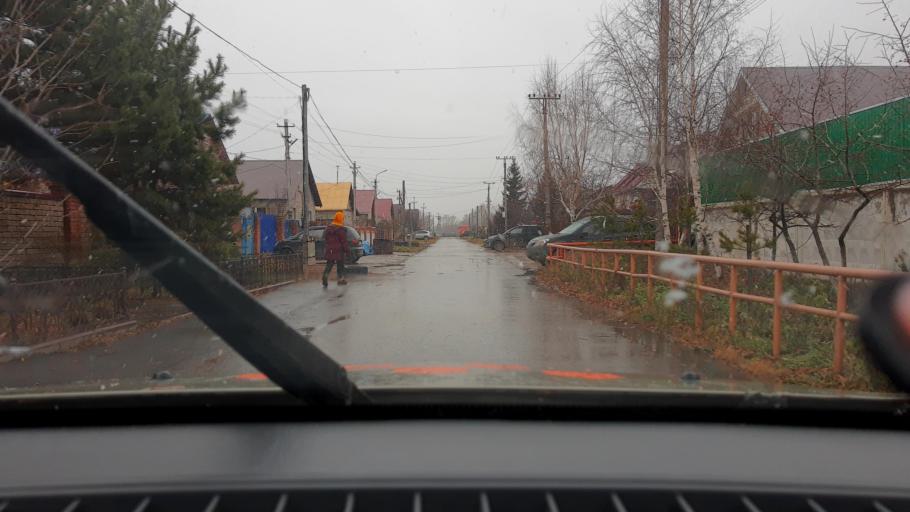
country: RU
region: Bashkortostan
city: Ufa
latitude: 54.6208
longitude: 55.9123
